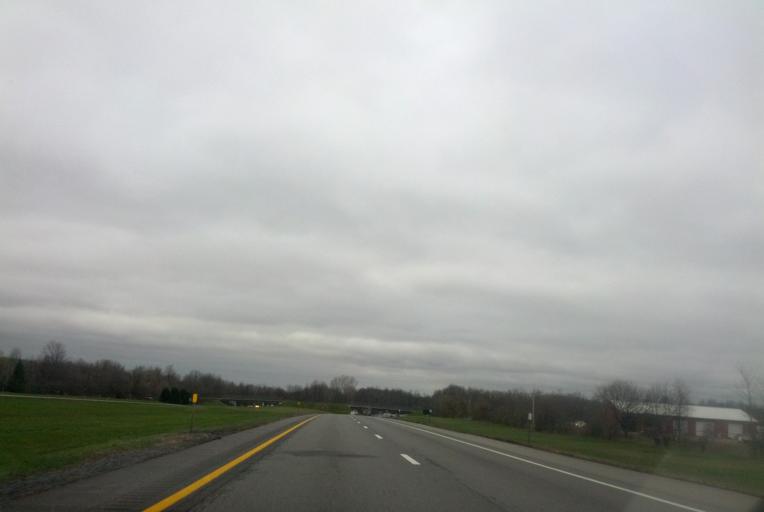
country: US
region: New York
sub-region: Ontario County
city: Clifton Springs
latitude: 42.9739
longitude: -77.1737
